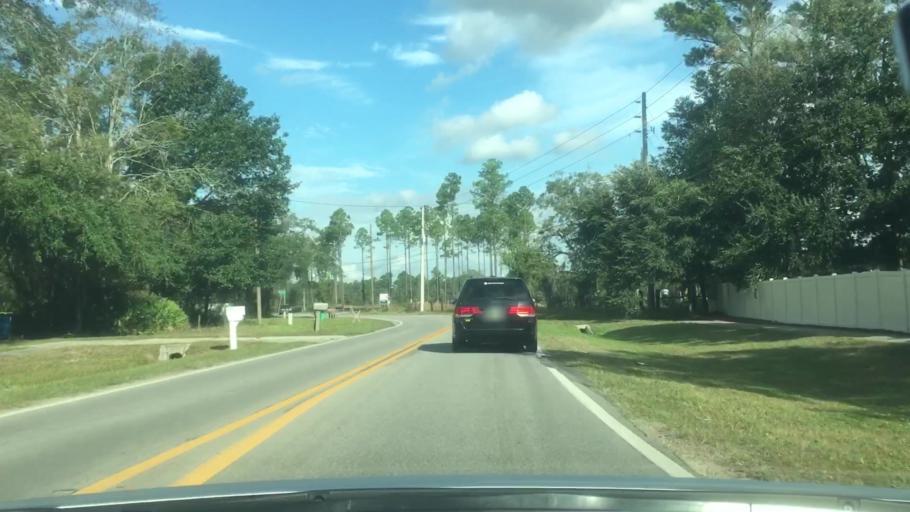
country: US
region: Florida
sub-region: Nassau County
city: Yulee
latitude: 30.4986
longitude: -81.5755
